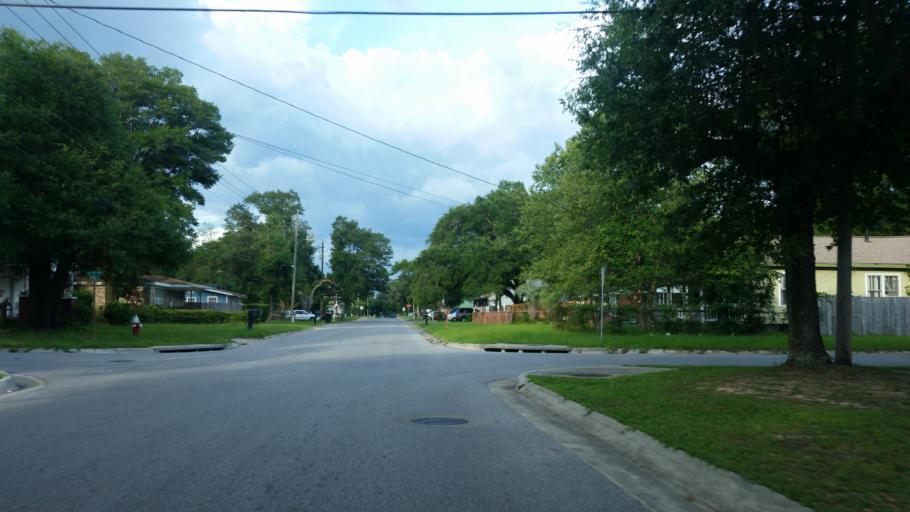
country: US
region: Florida
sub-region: Escambia County
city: Goulding
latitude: 30.4443
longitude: -87.2091
